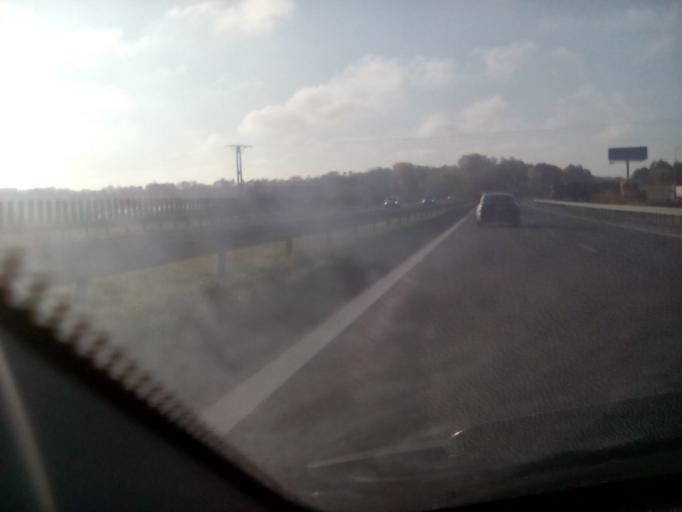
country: PL
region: Masovian Voivodeship
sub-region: Powiat grojecki
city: Grojec
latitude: 51.8806
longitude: 20.8558
